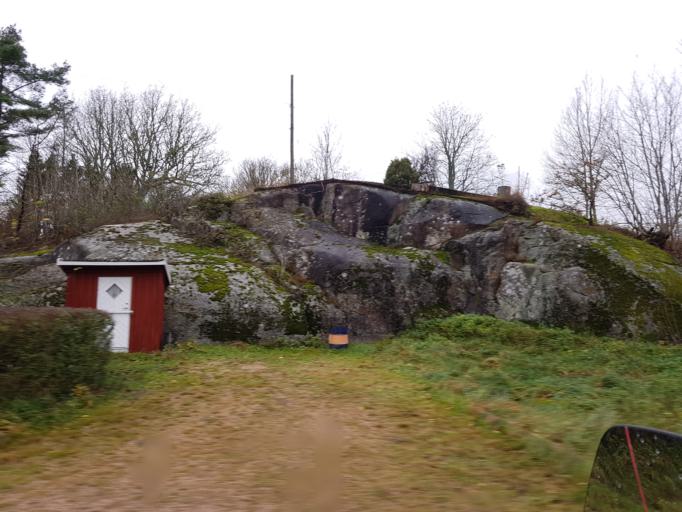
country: SE
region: Vaestra Goetaland
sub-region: Orust
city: Henan
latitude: 58.2078
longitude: 11.7640
